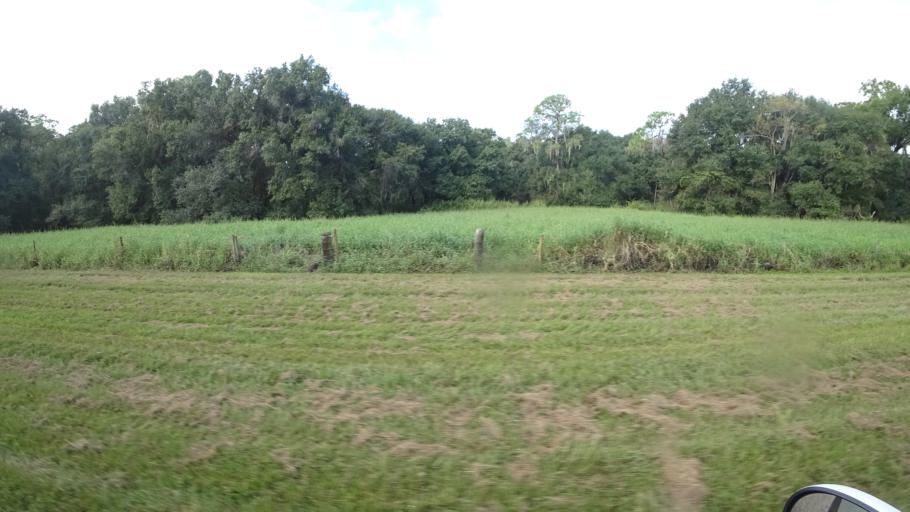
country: US
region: Florida
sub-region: Hillsborough County
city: Wimauma
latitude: 27.5942
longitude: -82.3378
